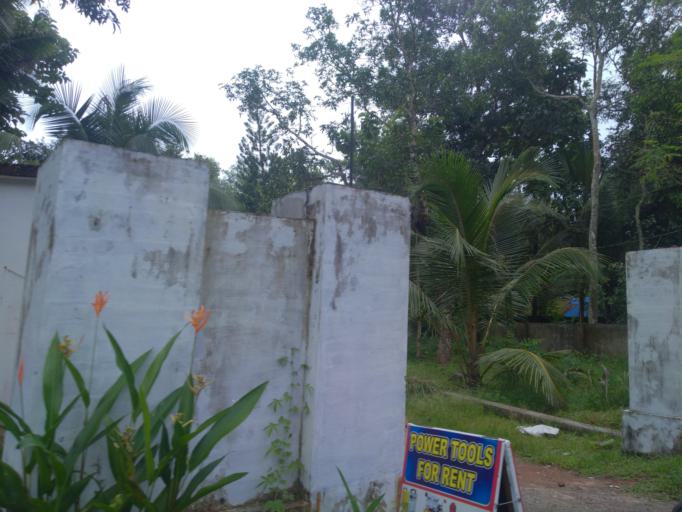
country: IN
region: Kerala
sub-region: Alappuzha
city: Shertallai
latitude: 9.6190
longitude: 76.3603
